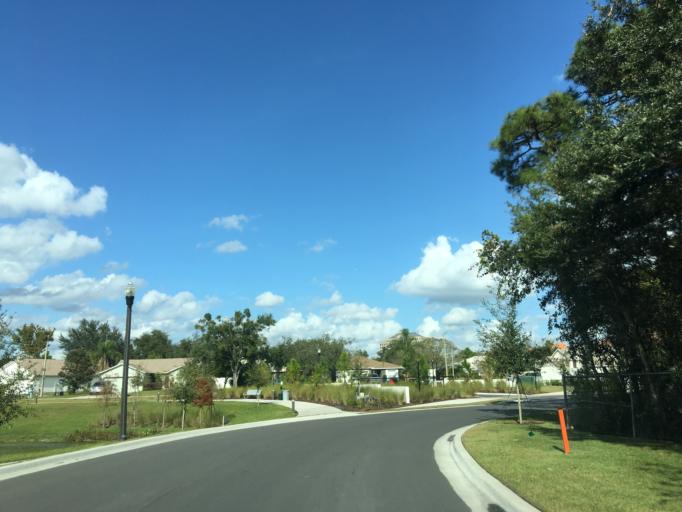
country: US
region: Florida
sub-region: Orange County
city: Eatonville
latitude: 28.6268
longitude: -81.4057
